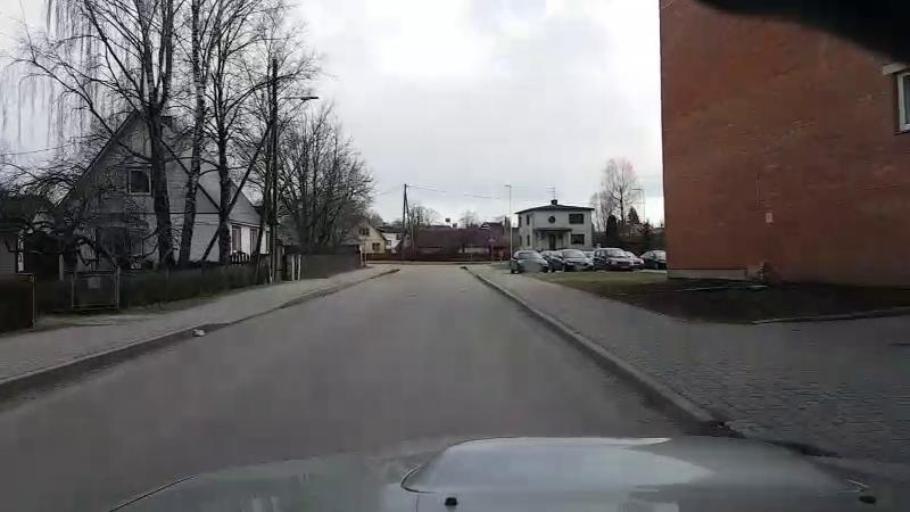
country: EE
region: Jaervamaa
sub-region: Paide linn
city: Paide
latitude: 58.8916
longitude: 25.5636
